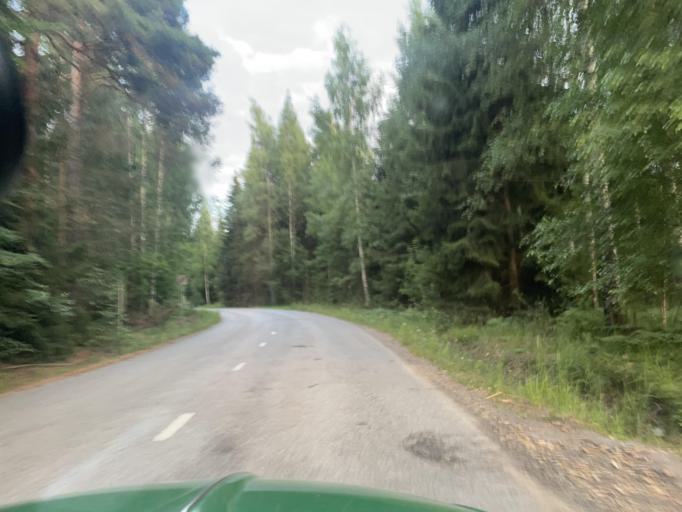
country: FI
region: Uusimaa
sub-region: Helsinki
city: Lohja
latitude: 60.2344
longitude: 24.0691
